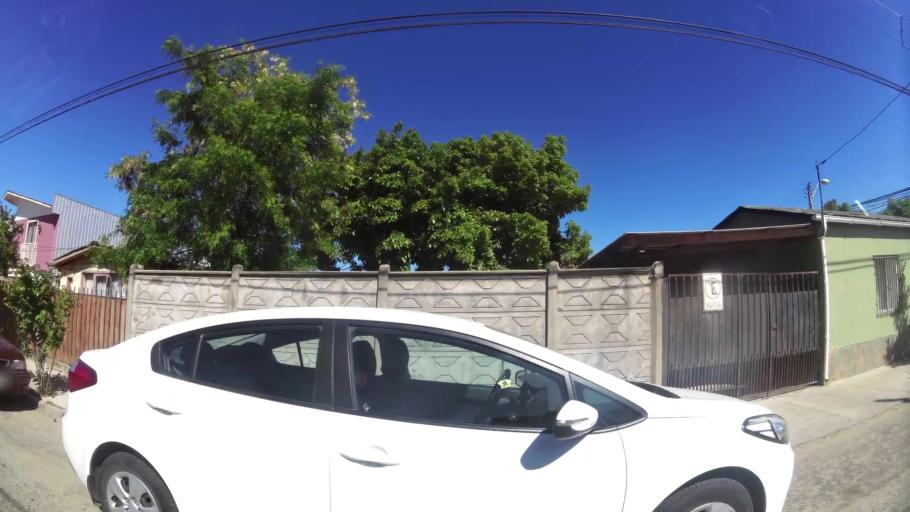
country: CL
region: Valparaiso
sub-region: Provincia de Marga Marga
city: Quilpue
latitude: -33.3199
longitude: -71.4080
